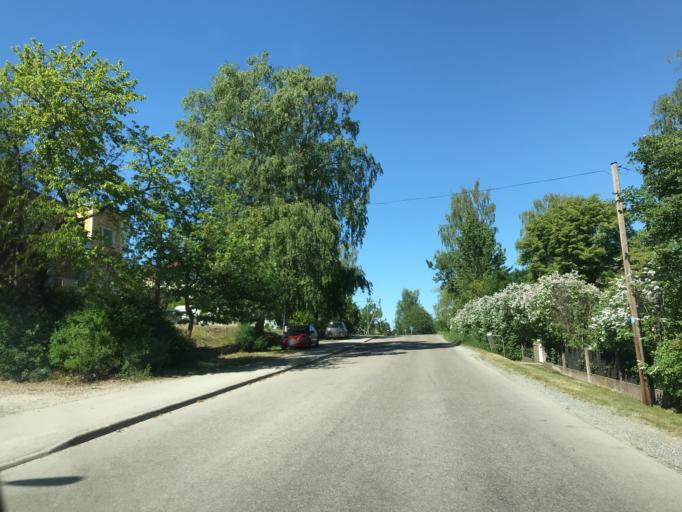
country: SE
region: Stockholm
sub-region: Sollentuna Kommun
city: Sollentuna
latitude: 59.4151
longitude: 17.9728
